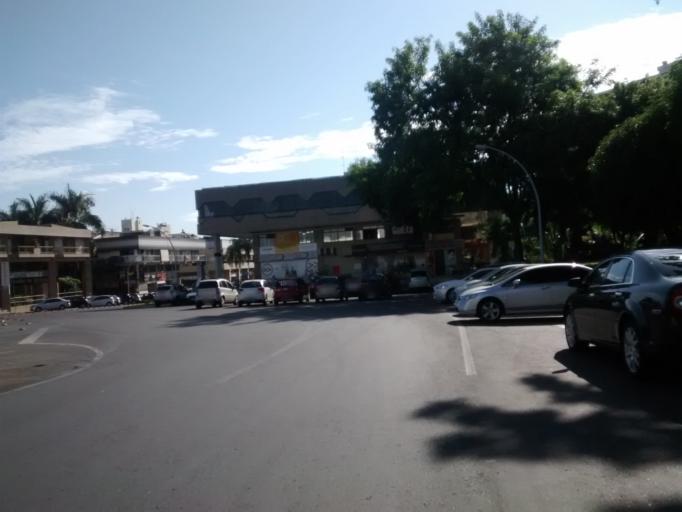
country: BR
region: Federal District
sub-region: Brasilia
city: Brasilia
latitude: -15.7572
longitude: -47.8922
